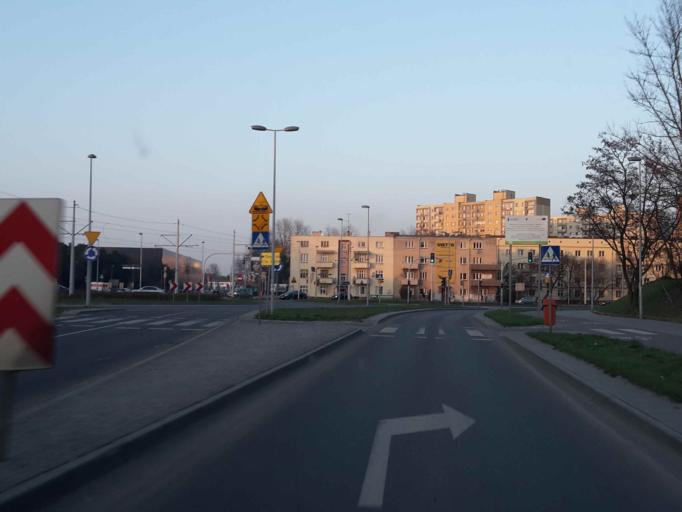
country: PL
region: Kujawsko-Pomorskie
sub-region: Torun
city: Torun
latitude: 53.0144
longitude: 18.5840
